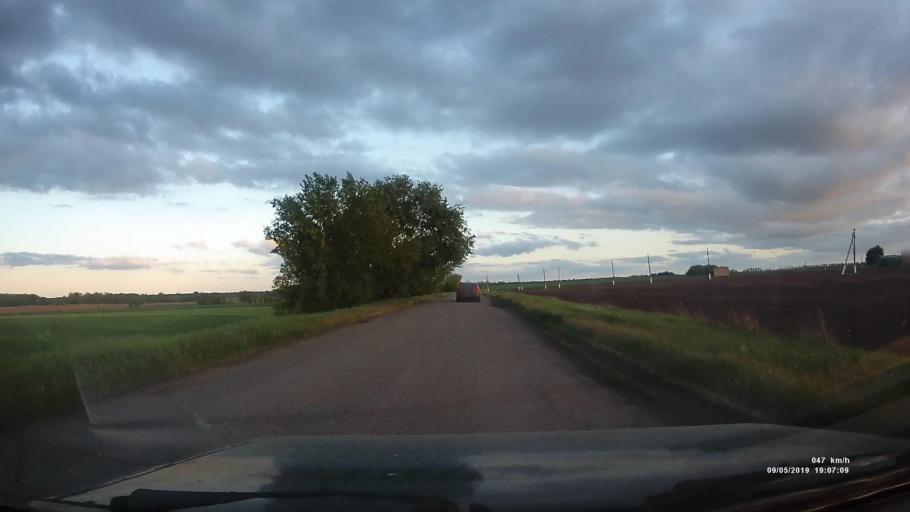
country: RU
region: Krasnodarskiy
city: Kanelovskaya
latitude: 46.7358
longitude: 39.1965
